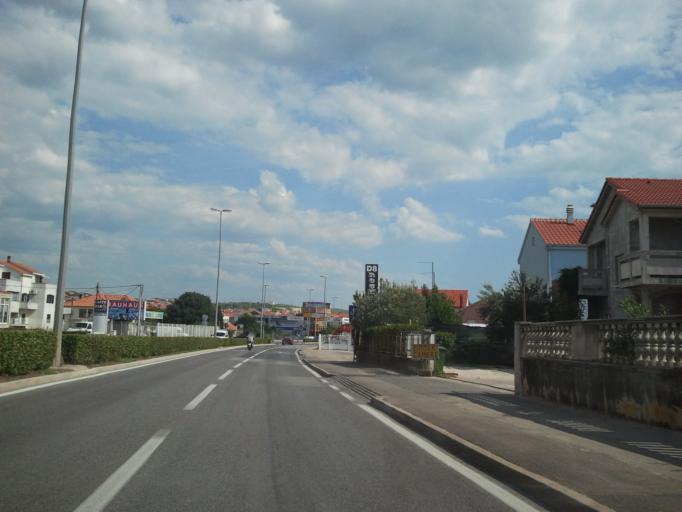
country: HR
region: Zadarska
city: Zadar
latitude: 44.1103
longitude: 15.2580
